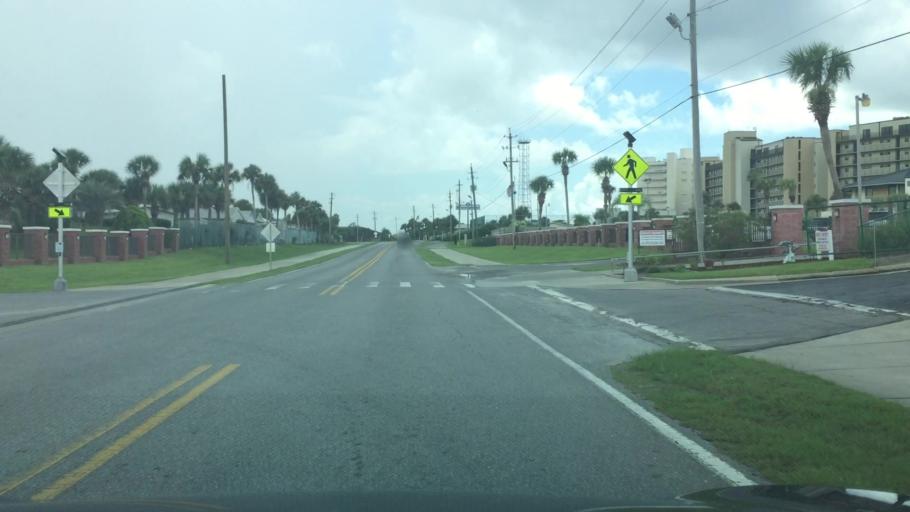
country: US
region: Florida
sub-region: Bay County
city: Lower Grand Lagoon
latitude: 30.1367
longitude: -85.7473
